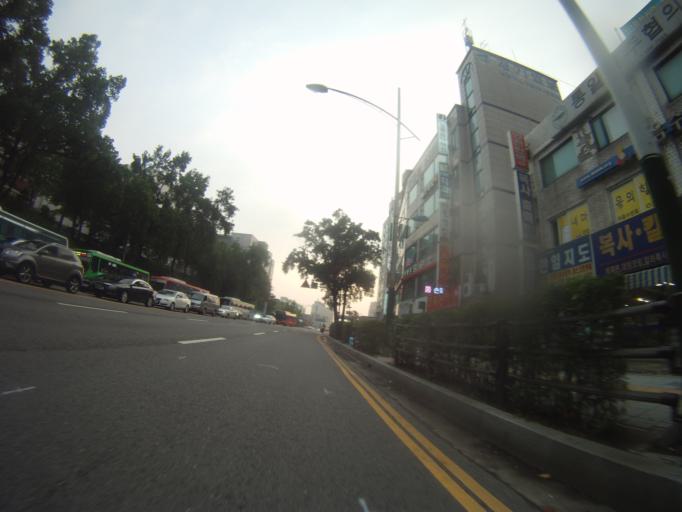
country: KR
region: Incheon
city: Incheon
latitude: 37.4575
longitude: 126.6929
